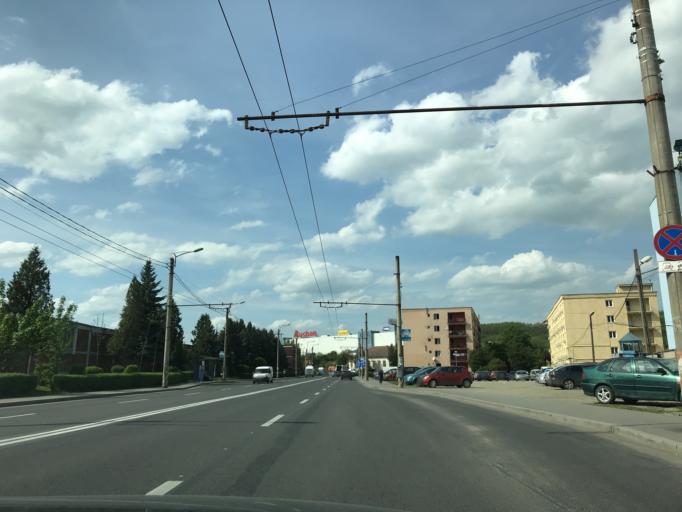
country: RO
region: Cluj
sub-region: Municipiul Cluj-Napoca
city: Cluj-Napoca
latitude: 46.7959
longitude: 23.6135
